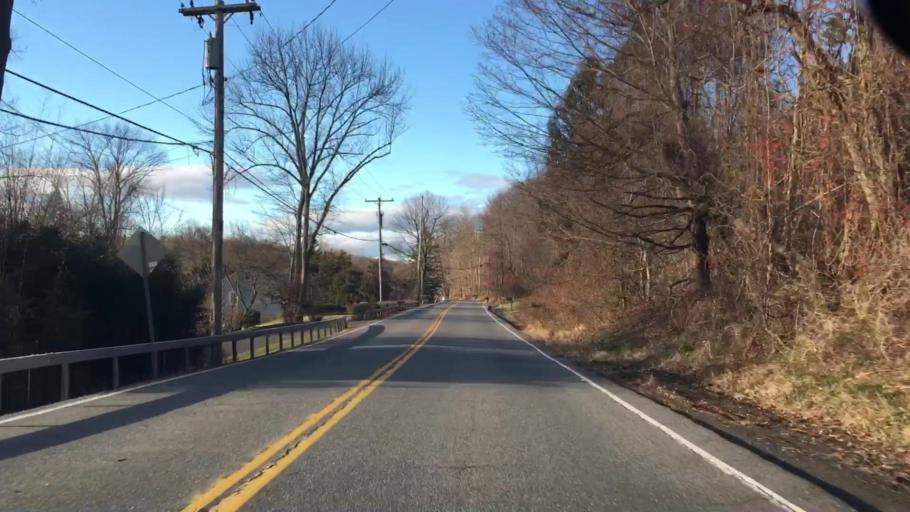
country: US
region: New York
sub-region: Putnam County
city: Lake Carmel
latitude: 41.4757
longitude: -73.6457
